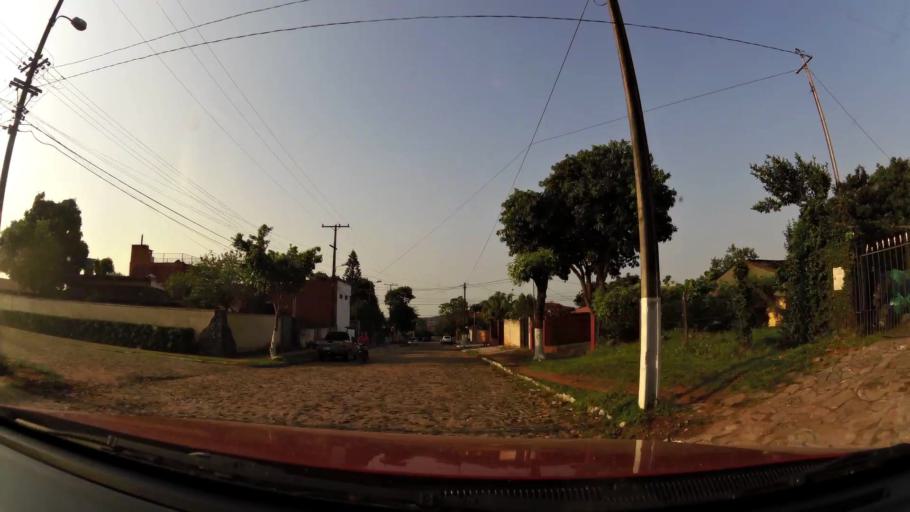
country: PY
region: Central
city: Lambare
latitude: -25.3533
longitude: -57.6107
